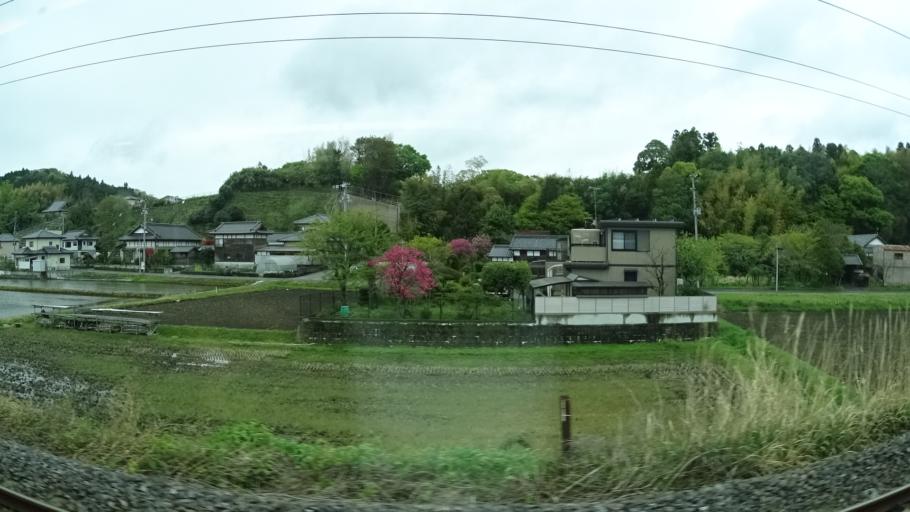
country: JP
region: Fukushima
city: Iwaki
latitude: 36.9803
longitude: 140.8634
